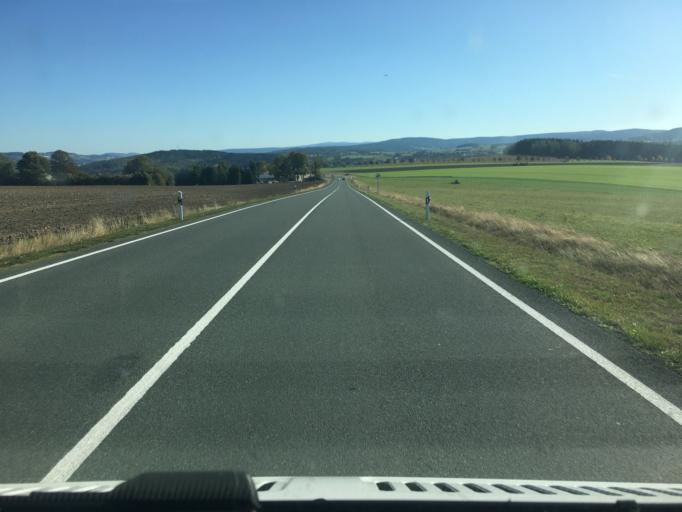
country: DE
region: Saxony
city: Schneeberg
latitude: 50.6053
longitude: 12.6050
